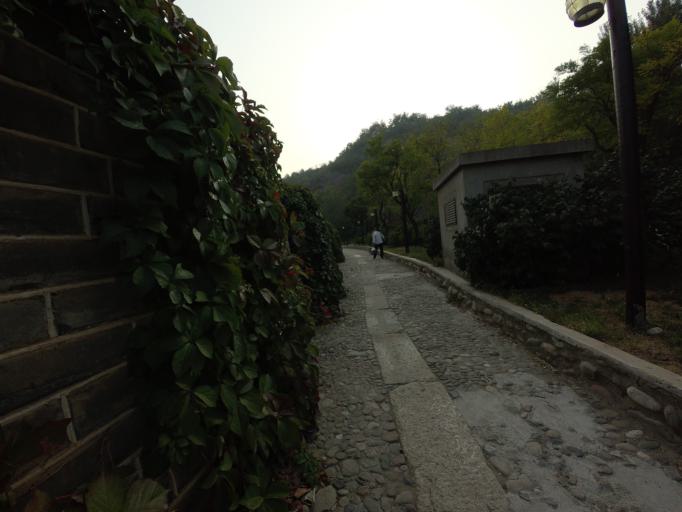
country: CN
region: Beijing
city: Xinchengzi
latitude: 40.6510
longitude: 117.2660
